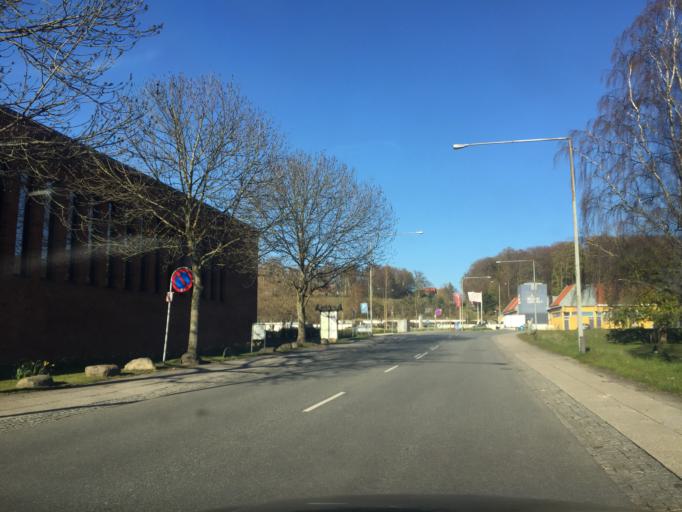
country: DK
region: Capital Region
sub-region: Halsnaes Kommune
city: Frederiksvaerk
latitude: 55.9761
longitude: 12.0168
